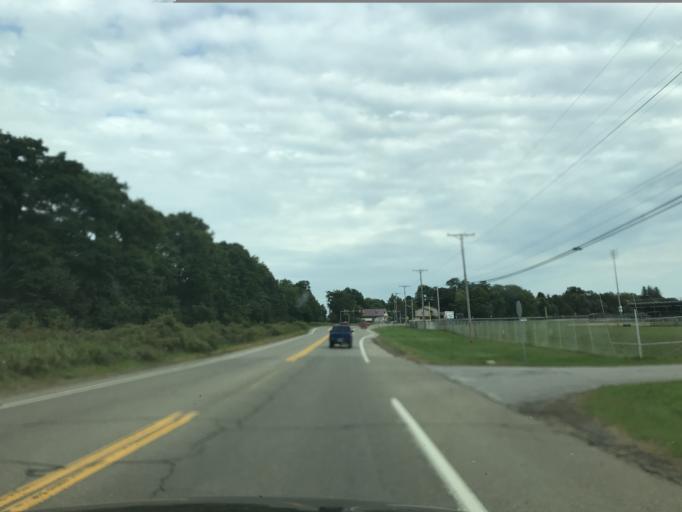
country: US
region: Pennsylvania
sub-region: Erie County
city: Northwest Harborcreek
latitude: 42.1650
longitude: -79.9575
